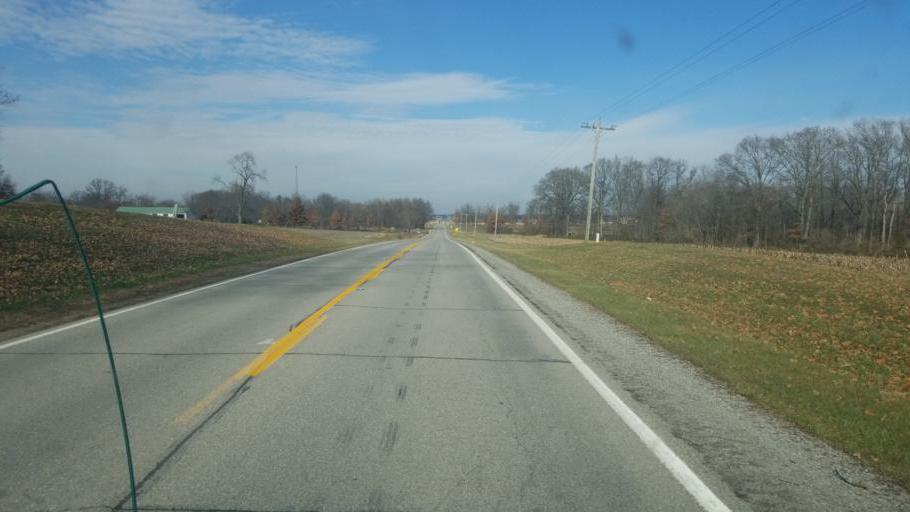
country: US
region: Illinois
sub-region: Saline County
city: Eldorado
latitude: 37.9266
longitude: -88.4576
